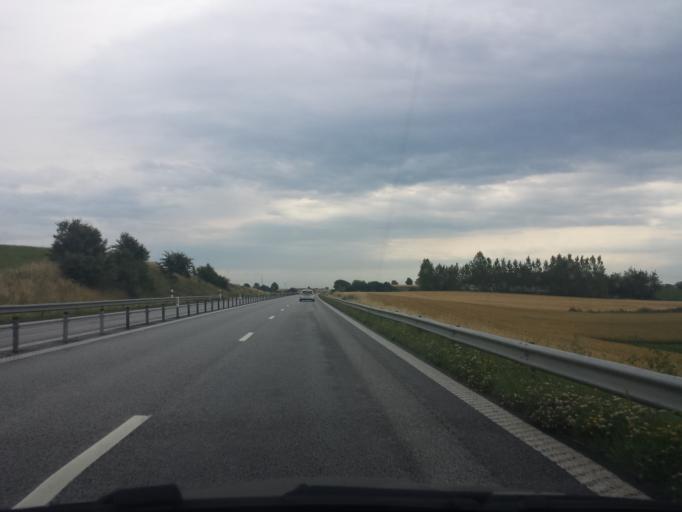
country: SE
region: Skane
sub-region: Skurups Kommun
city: Rydsgard
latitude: 55.4820
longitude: 13.6066
